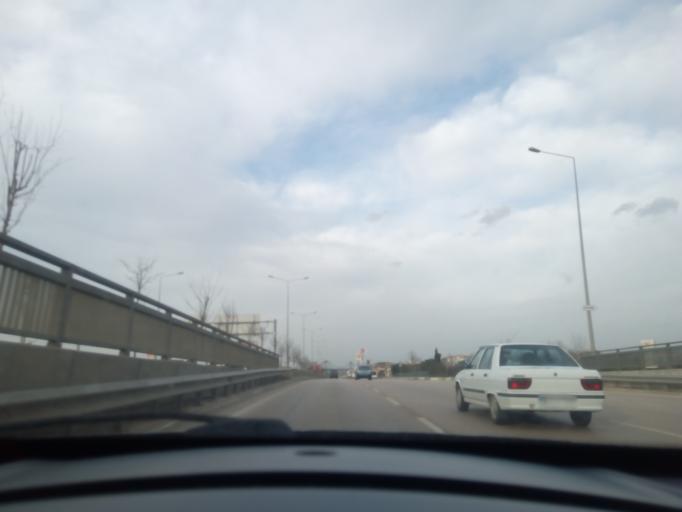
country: TR
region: Bursa
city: Cali
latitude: 40.2122
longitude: 28.9347
